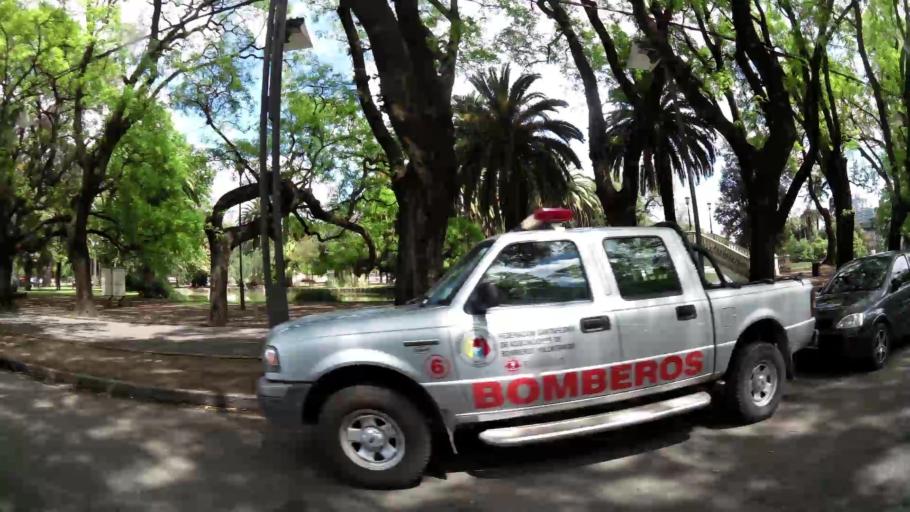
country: AR
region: Santa Fe
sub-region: Departamento de Rosario
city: Rosario
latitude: -32.9577
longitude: -60.6569
